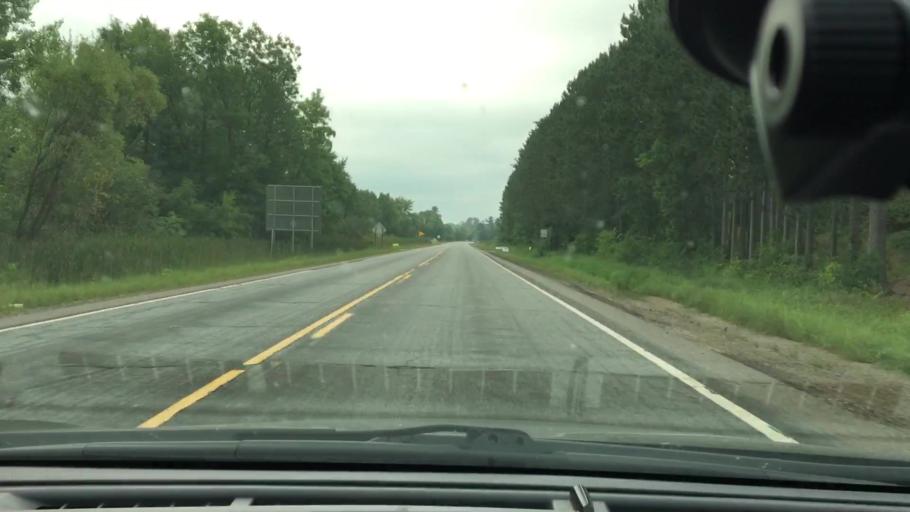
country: US
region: Minnesota
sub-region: Crow Wing County
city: Cross Lake
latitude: 46.7220
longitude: -93.9572
